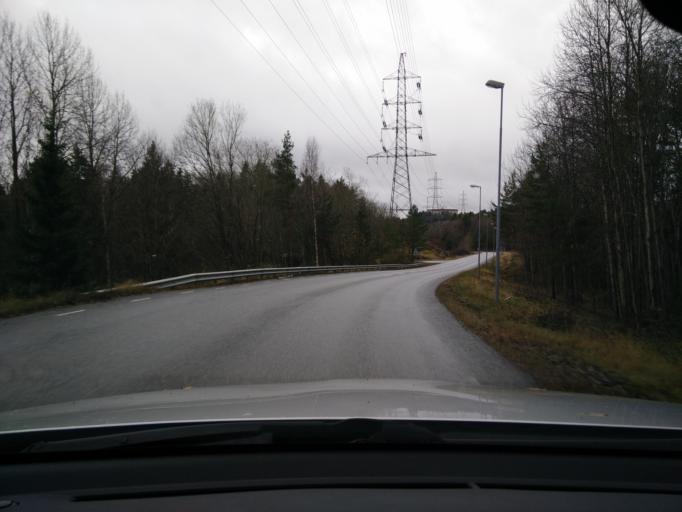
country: SE
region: Stockholm
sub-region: Sollentuna Kommun
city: Sollentuna
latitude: 59.4576
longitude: 17.9621
